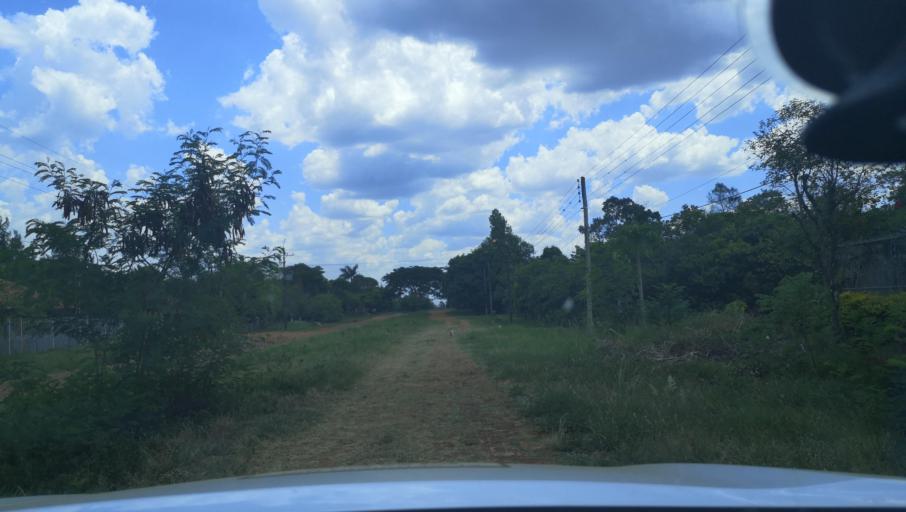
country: PY
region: Itapua
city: Carmen del Parana
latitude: -27.1713
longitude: -56.2304
